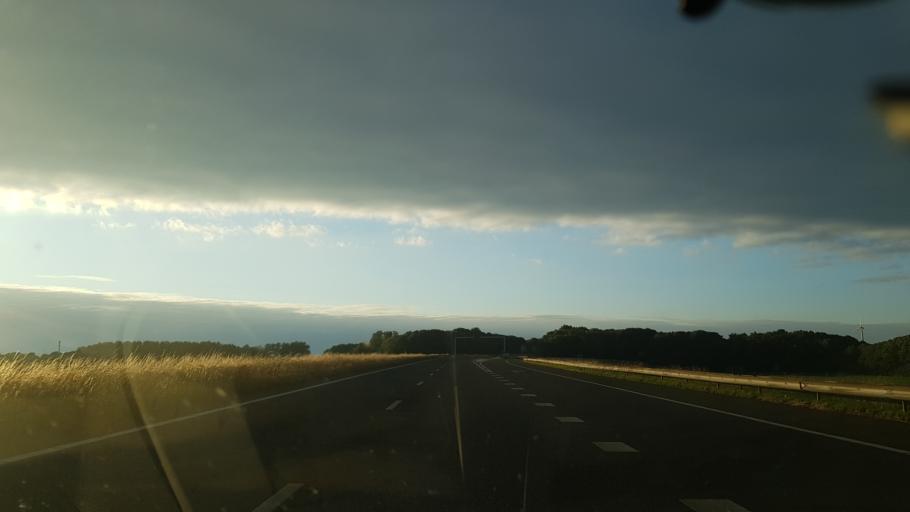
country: NL
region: North Holland
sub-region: Gemeente Hollands Kroon
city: Den Oever
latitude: 52.9236
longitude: 5.0358
